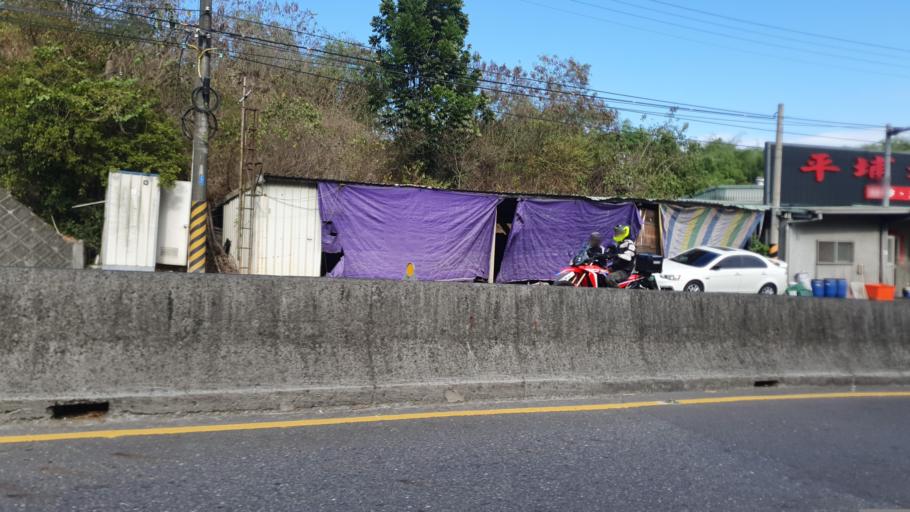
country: TW
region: Taiwan
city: Yujing
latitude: 23.0559
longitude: 120.4010
